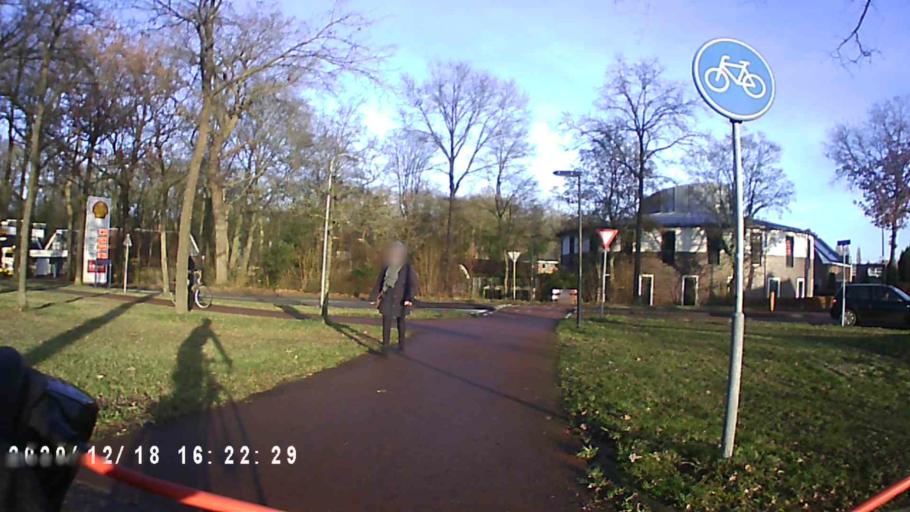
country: NL
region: Drenthe
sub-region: Gemeente Tynaarlo
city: Zuidlaren
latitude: 53.0912
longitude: 6.6905
